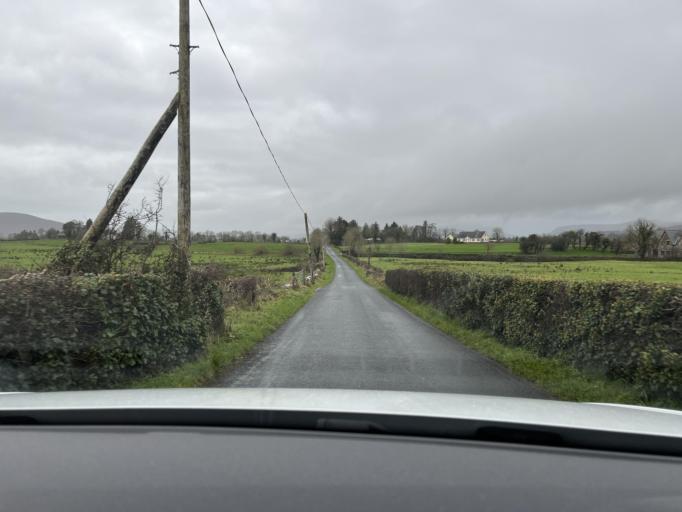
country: IE
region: Connaught
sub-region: County Leitrim
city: Manorhamilton
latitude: 54.2977
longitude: -8.1419
